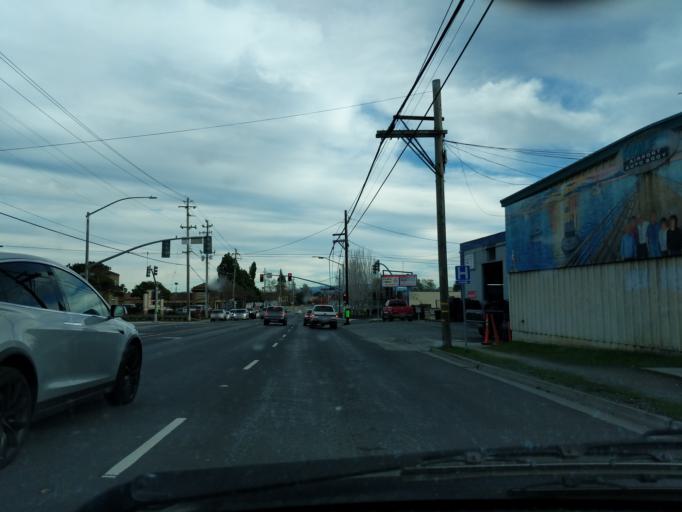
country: US
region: California
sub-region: Santa Cruz County
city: Freedom
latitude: 36.9387
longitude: -121.7787
